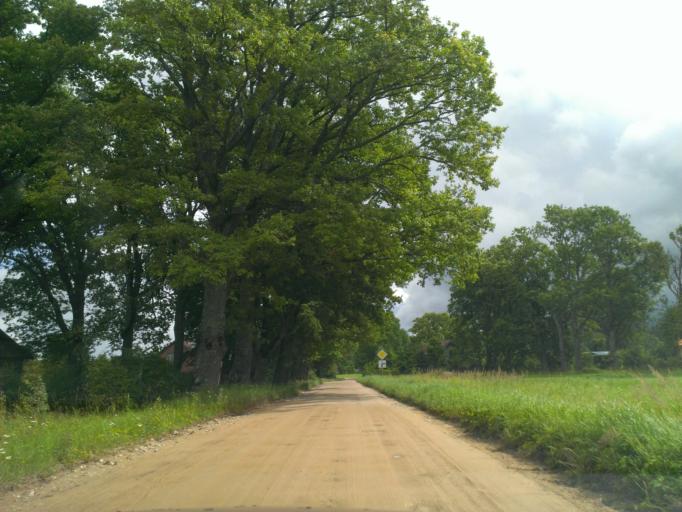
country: LV
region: Ligatne
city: Ligatne
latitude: 57.2018
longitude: 24.9817
